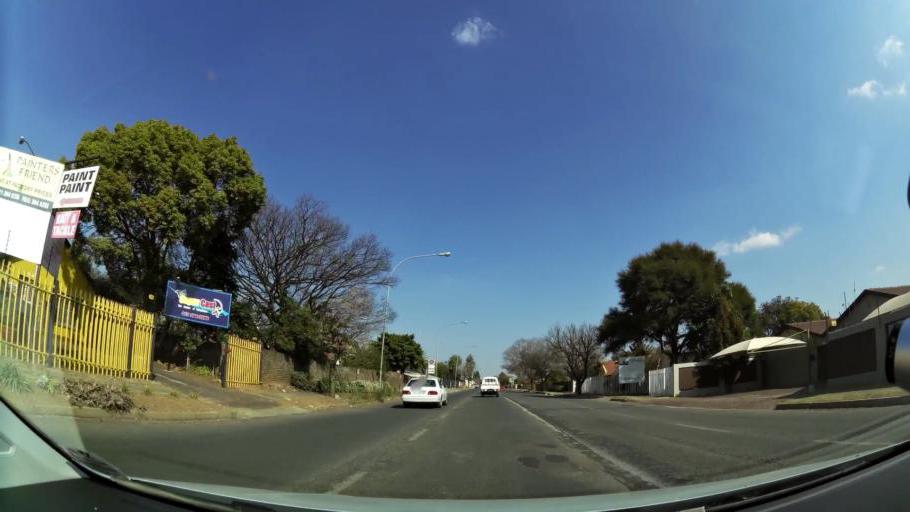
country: ZA
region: Gauteng
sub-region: City of Johannesburg Metropolitan Municipality
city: Modderfontein
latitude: -26.0863
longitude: 28.2394
